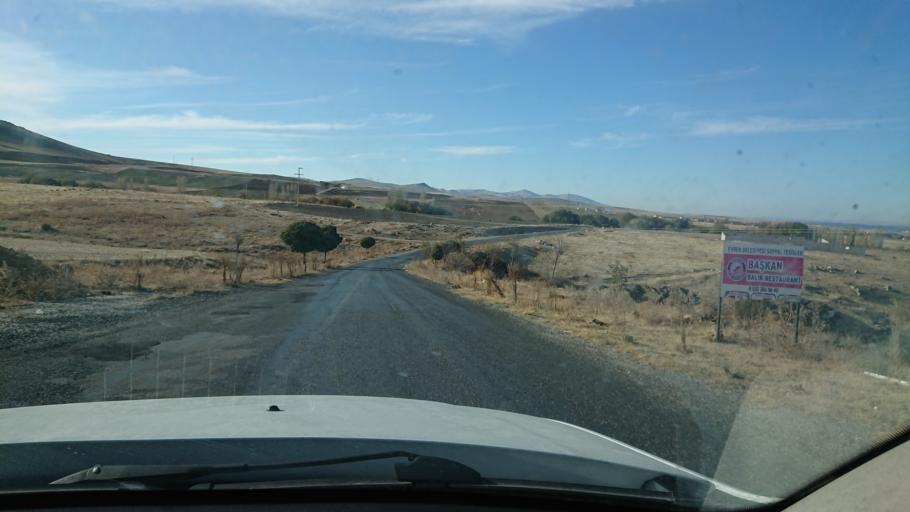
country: TR
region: Aksaray
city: Sariyahsi
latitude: 38.9682
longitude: 33.8705
